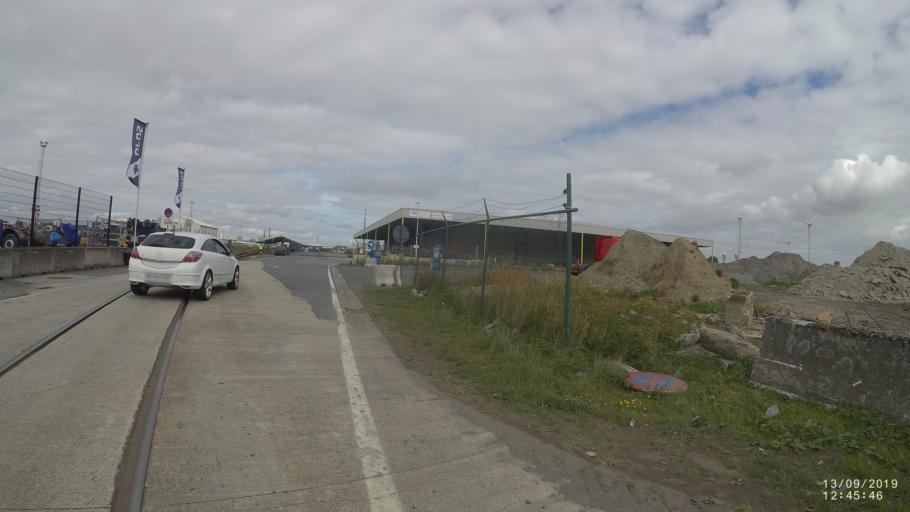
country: BE
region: Flanders
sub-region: Provincie Oost-Vlaanderen
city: Evergem
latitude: 51.1133
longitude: 3.7619
